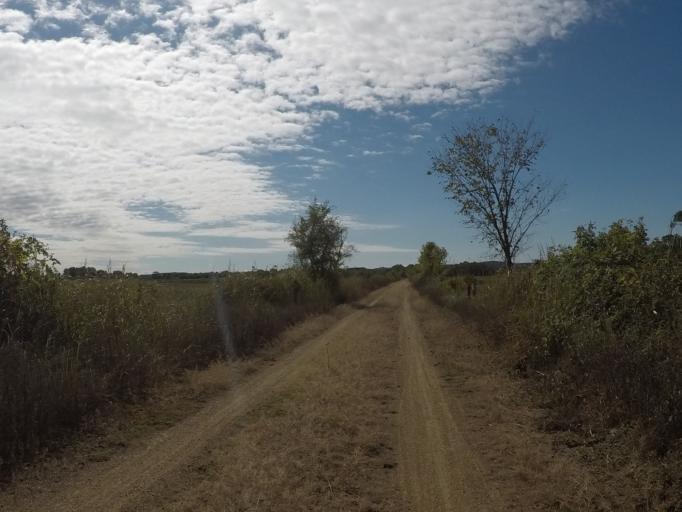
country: US
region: Wisconsin
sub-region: Richland County
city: Richland Center
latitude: 43.2372
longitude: -90.3007
